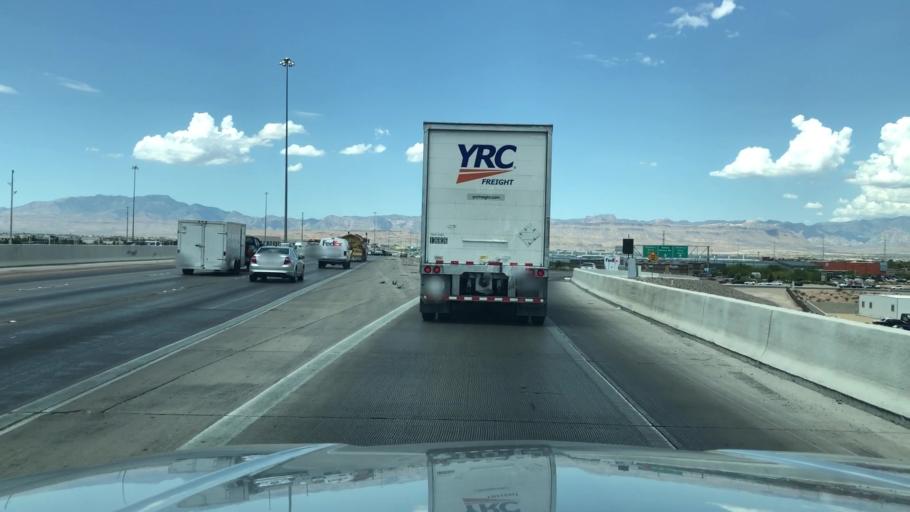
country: US
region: Nevada
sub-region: Clark County
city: Spring Valley
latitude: 36.0686
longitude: -115.2040
